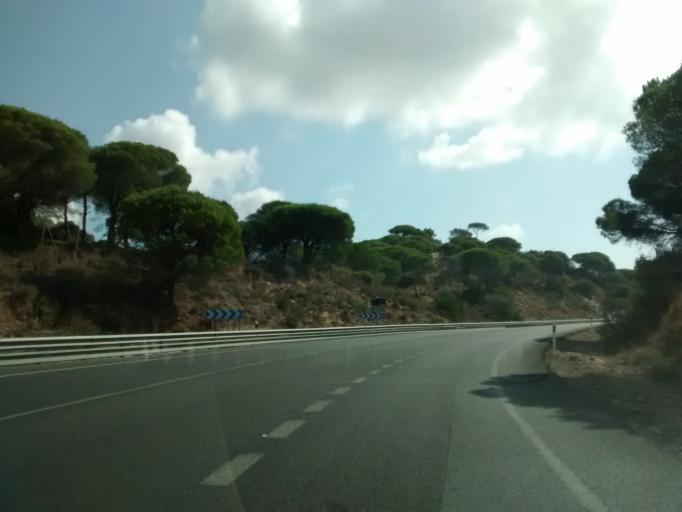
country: ES
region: Andalusia
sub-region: Provincia de Cadiz
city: Vejer de la Frontera
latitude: 36.2556
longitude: -5.9472
